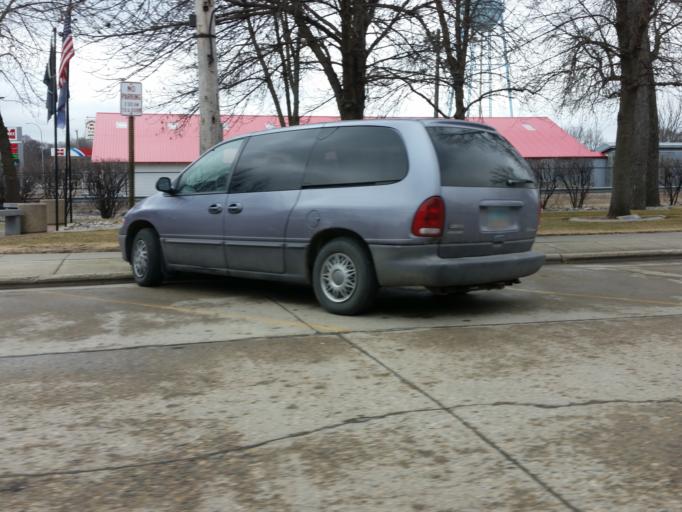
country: US
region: North Dakota
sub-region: Cass County
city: Casselton
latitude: 46.9006
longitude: -97.2118
